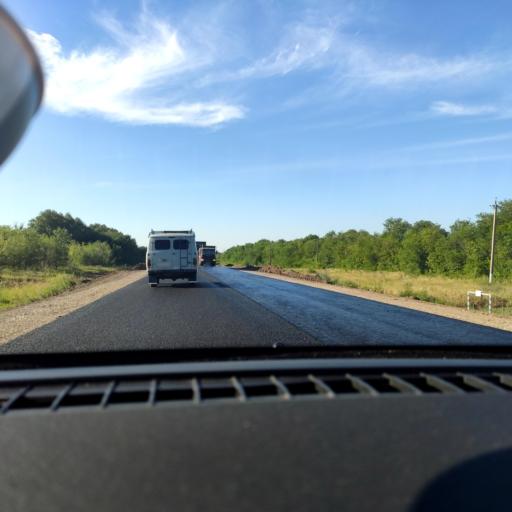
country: RU
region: Samara
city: Krasnoarmeyskoye
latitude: 52.8099
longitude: 50.0121
